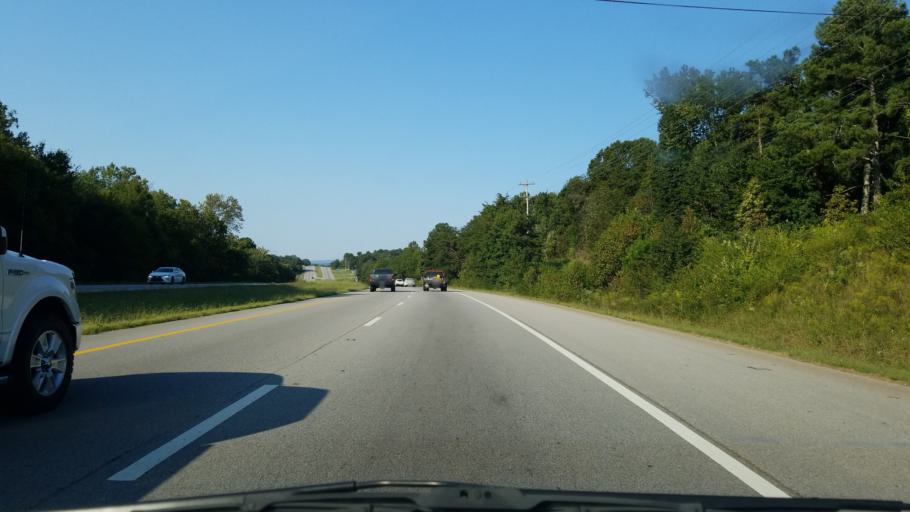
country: US
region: Tennessee
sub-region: Hamilton County
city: Harrison
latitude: 35.1033
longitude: -85.1649
